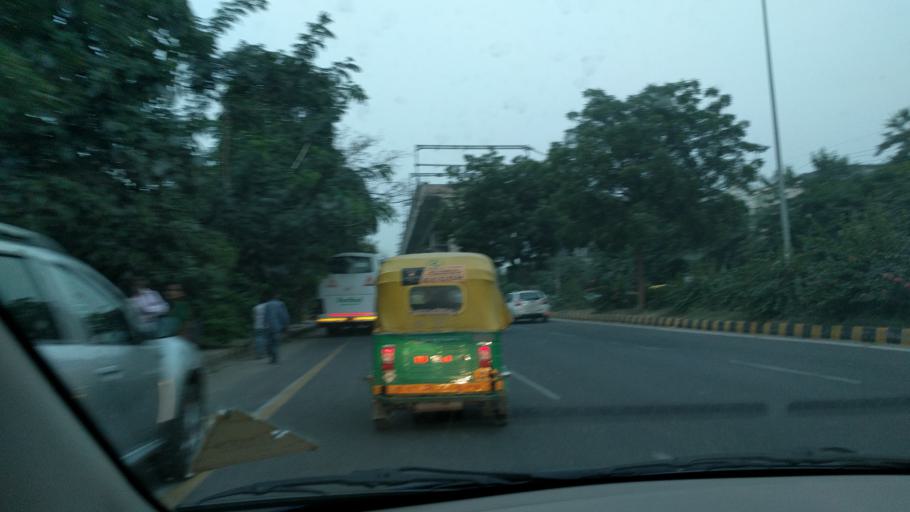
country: IN
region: Haryana
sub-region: Gurgaon
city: Gurgaon
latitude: 28.4538
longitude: 77.0676
